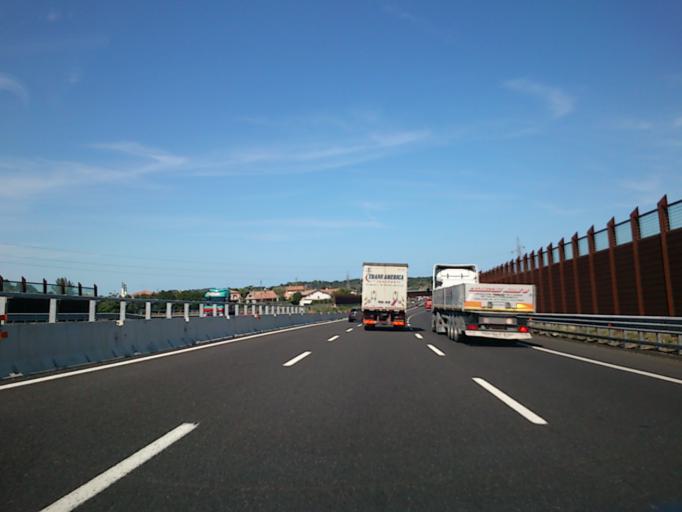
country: IT
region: The Marches
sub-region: Provincia di Pesaro e Urbino
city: Rosciano
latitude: 43.8249
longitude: 12.9980
